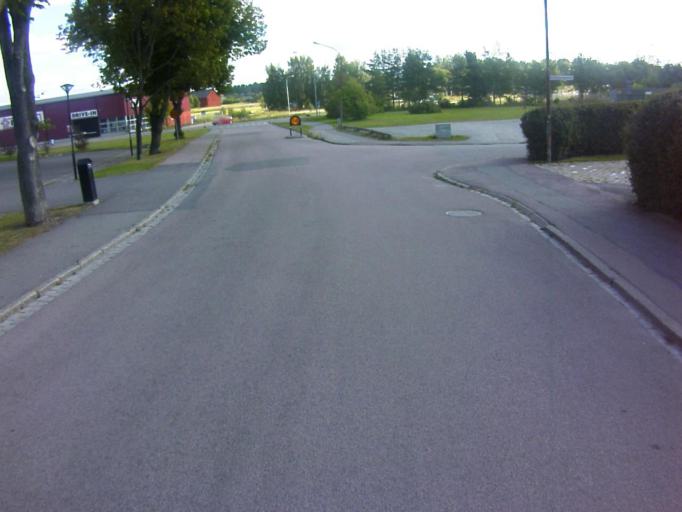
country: SE
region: Soedermanland
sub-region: Eskilstuna Kommun
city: Eskilstuna
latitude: 59.3734
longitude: 16.5420
